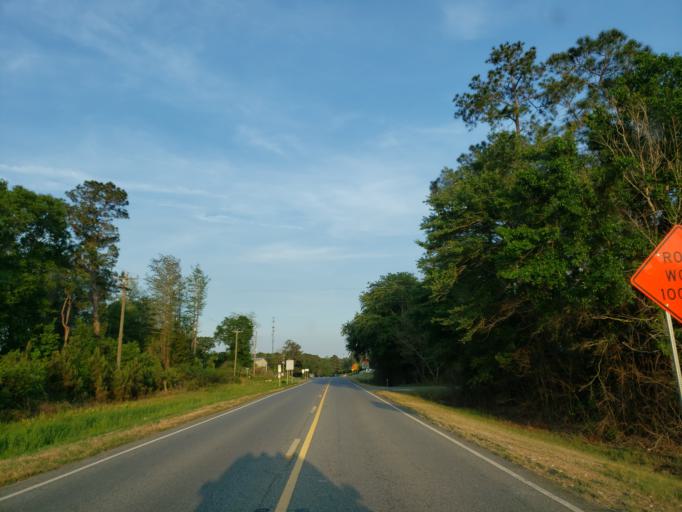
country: US
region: Georgia
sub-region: Lowndes County
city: Hahira
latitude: 30.9947
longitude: -83.4008
